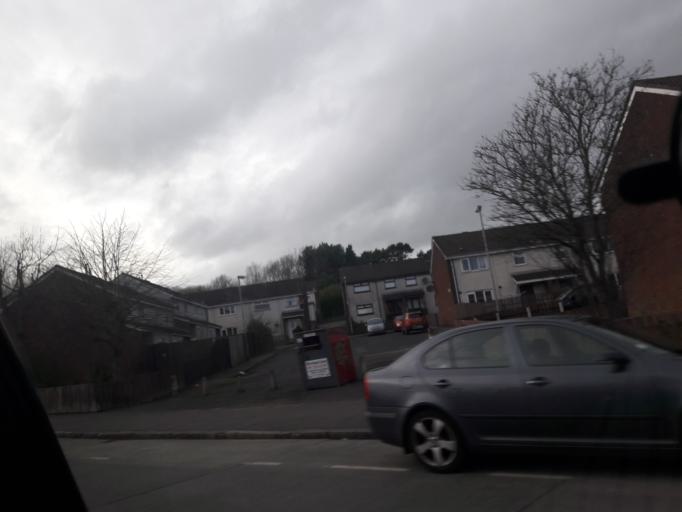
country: GB
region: Northern Ireland
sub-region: City of Belfast
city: Belfast
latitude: 54.6259
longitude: -5.9456
